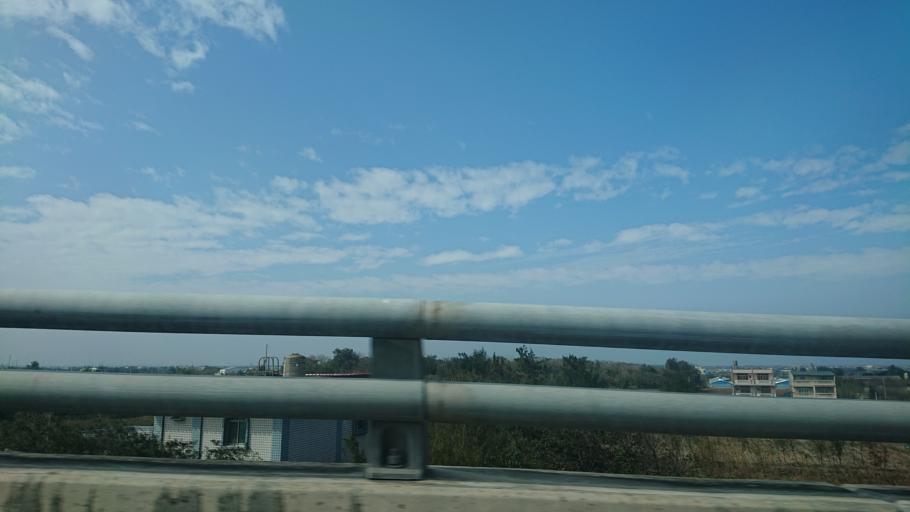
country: TW
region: Taiwan
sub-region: Yunlin
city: Douliu
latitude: 23.8581
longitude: 120.2959
